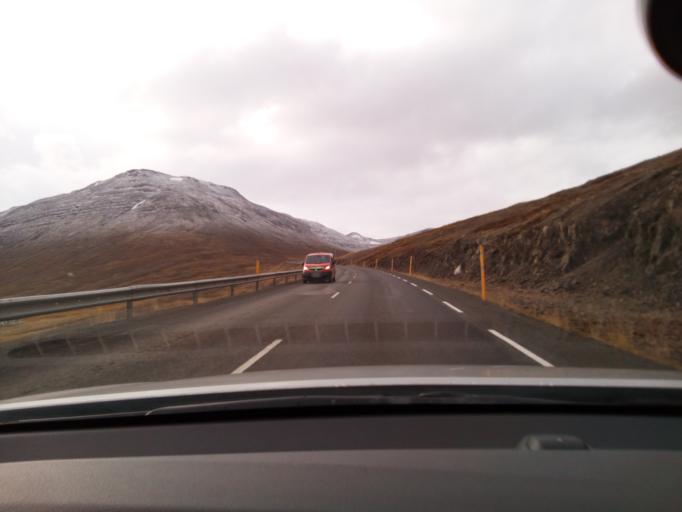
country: IS
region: Northeast
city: Dalvik
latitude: 65.4794
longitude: -18.6591
